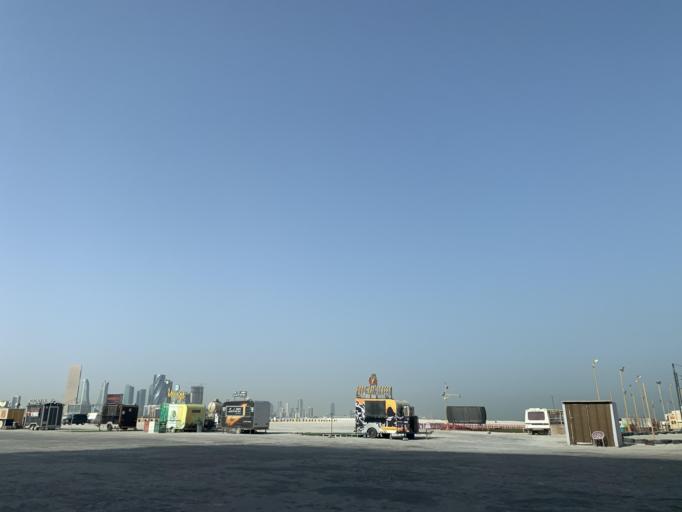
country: BH
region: Muharraq
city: Al Muharraq
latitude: 26.2647
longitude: 50.5942
